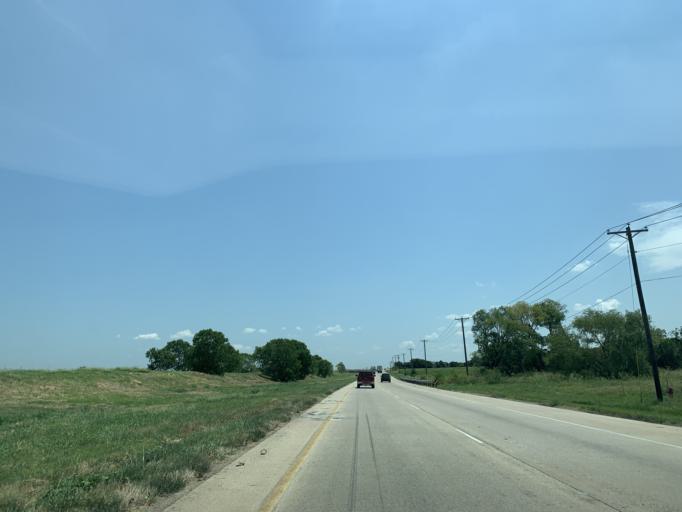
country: US
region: Texas
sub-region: Denton County
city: Roanoke
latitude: 33.0150
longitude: -97.2333
